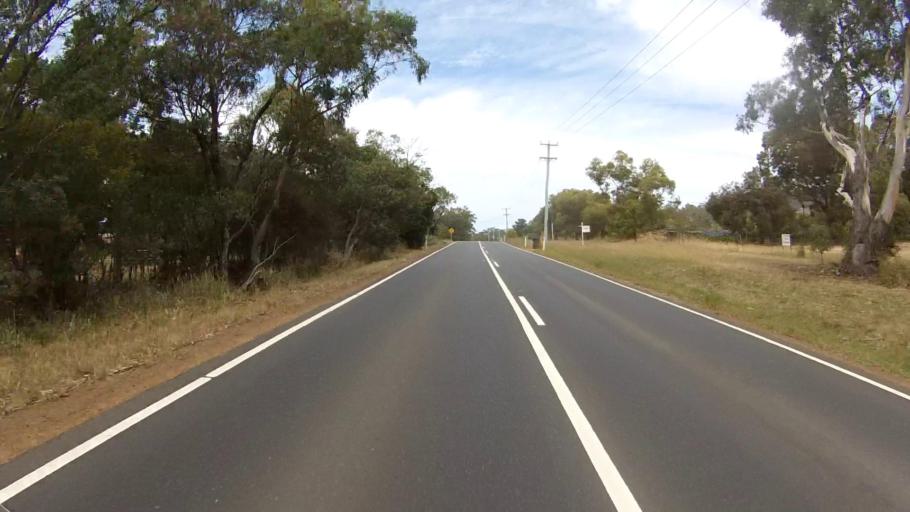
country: AU
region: Tasmania
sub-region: Clarence
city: Acton Park
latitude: -42.8858
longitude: 147.4832
